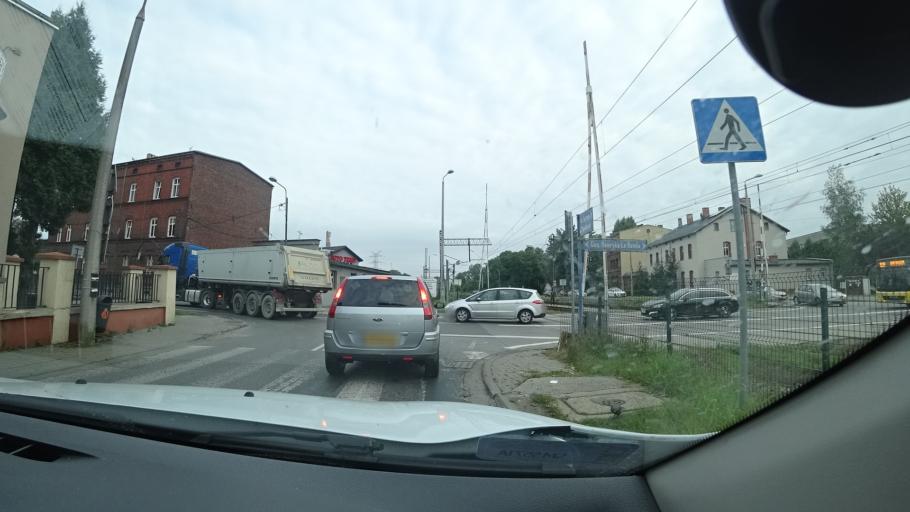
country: PL
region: Silesian Voivodeship
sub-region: Sosnowiec
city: Sosnowiec
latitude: 50.2766
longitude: 19.0657
